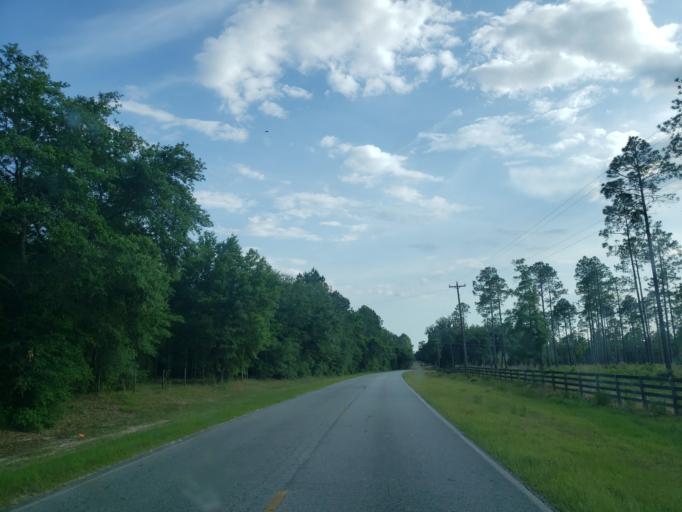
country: US
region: Georgia
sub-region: Echols County
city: Statenville
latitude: 30.6318
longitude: -83.1964
